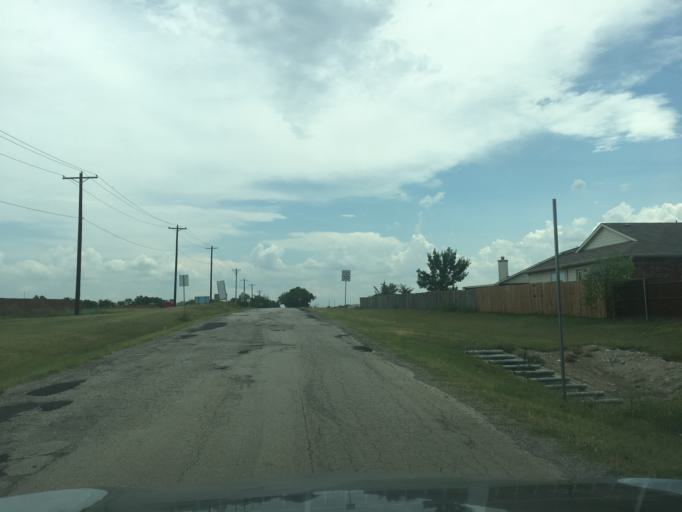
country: US
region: Texas
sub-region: Denton County
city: Argyle
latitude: 33.1731
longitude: -97.1679
